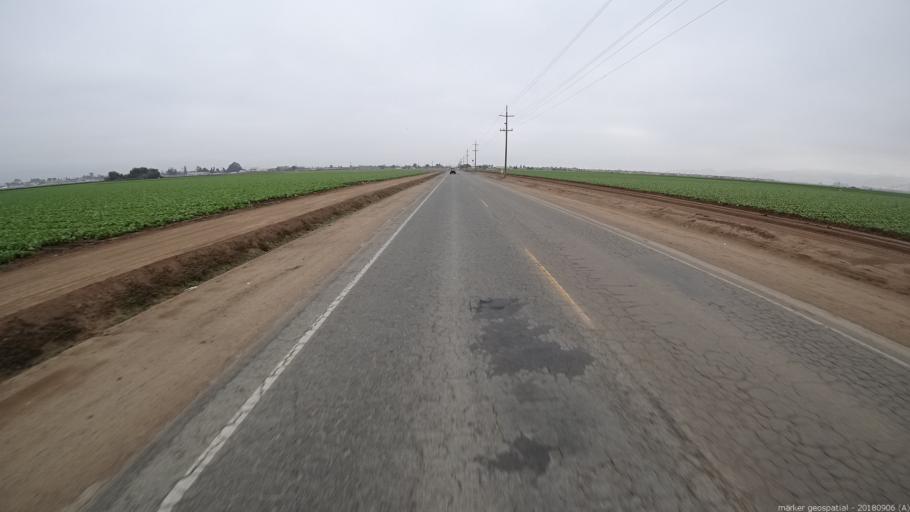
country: US
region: California
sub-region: Monterey County
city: Salinas
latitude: 36.6659
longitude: -121.5950
